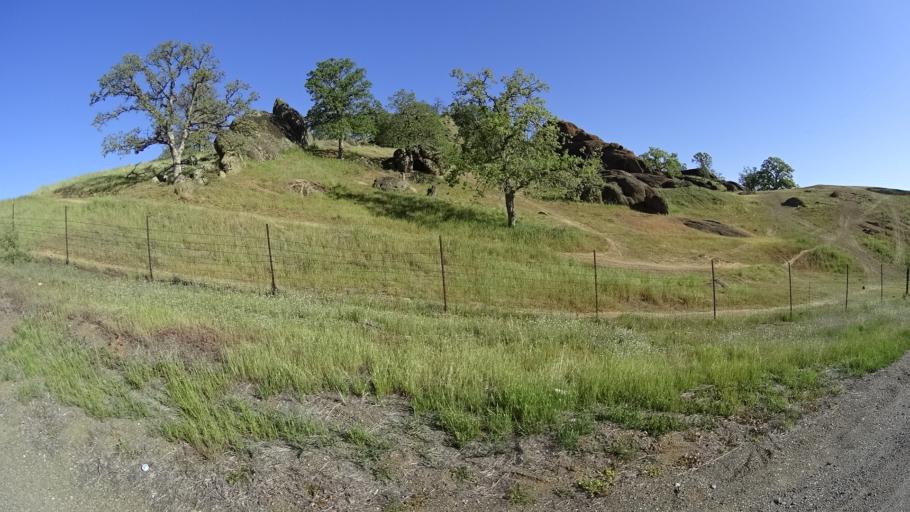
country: US
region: California
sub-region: Tehama County
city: Rancho Tehama Reserve
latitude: 39.7501
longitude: -122.5279
